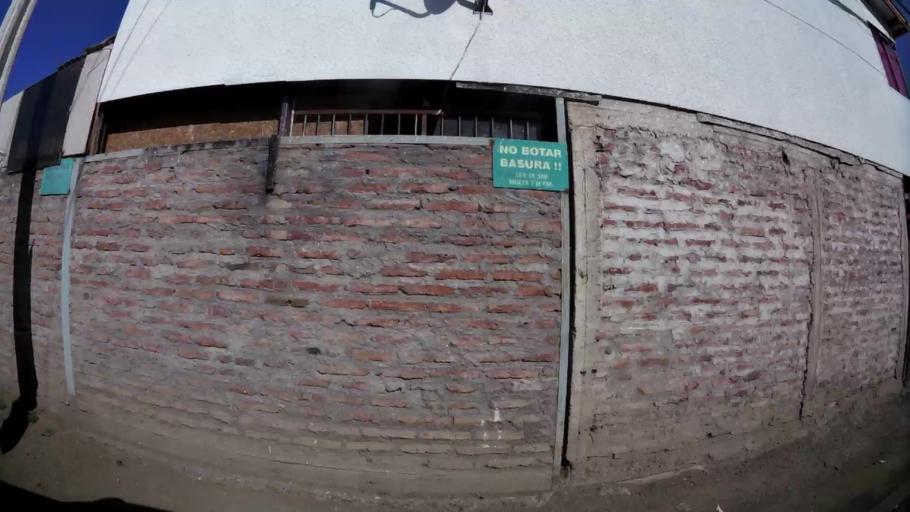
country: CL
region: Santiago Metropolitan
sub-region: Provincia de Santiago
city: Lo Prado
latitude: -33.4869
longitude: -70.7687
